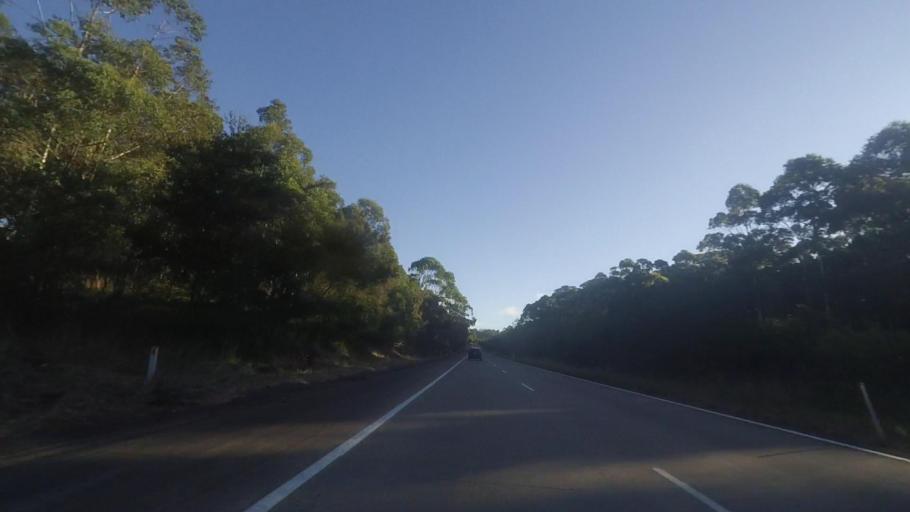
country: AU
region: New South Wales
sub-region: Great Lakes
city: Bulahdelah
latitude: -32.3076
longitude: 152.3451
